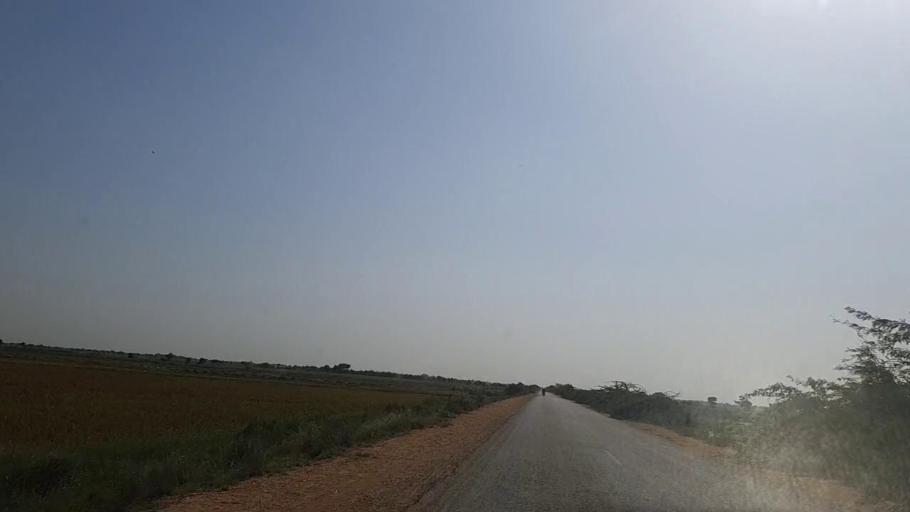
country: PK
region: Sindh
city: Mirpur Batoro
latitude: 24.5905
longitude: 68.2919
